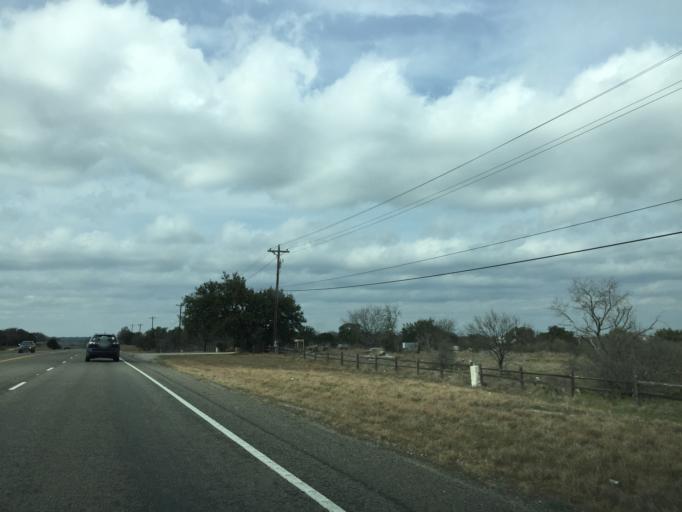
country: US
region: Texas
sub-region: Burnet County
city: Meadowlakes
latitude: 30.4917
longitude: -98.2314
